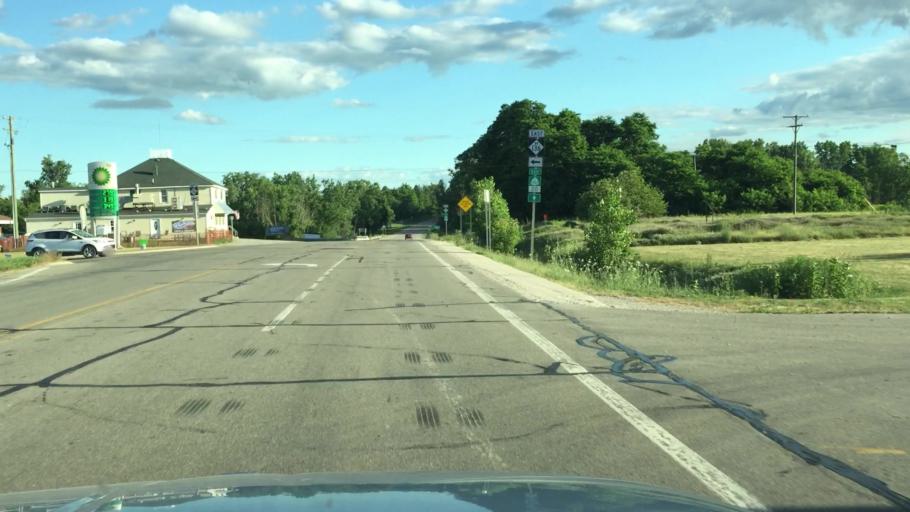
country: US
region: Michigan
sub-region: Saint Clair County
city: Yale
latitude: 43.0745
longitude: -82.7656
